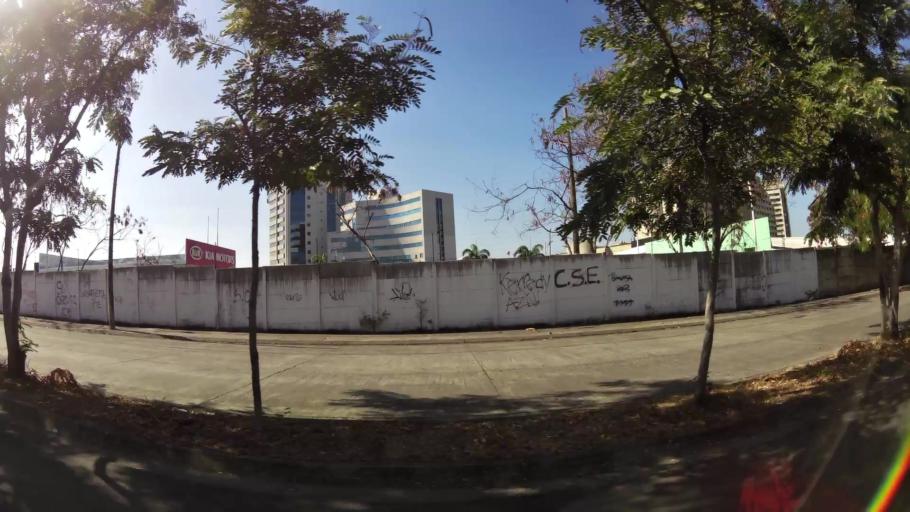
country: EC
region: Guayas
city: Eloy Alfaro
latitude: -2.1571
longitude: -79.8986
